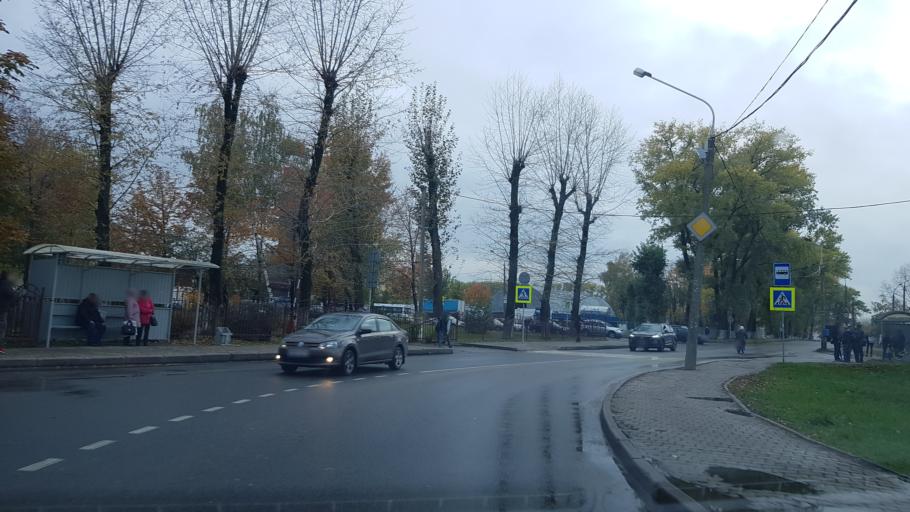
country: BY
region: Minsk
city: Syenitsa
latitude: 53.8436
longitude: 27.5449
